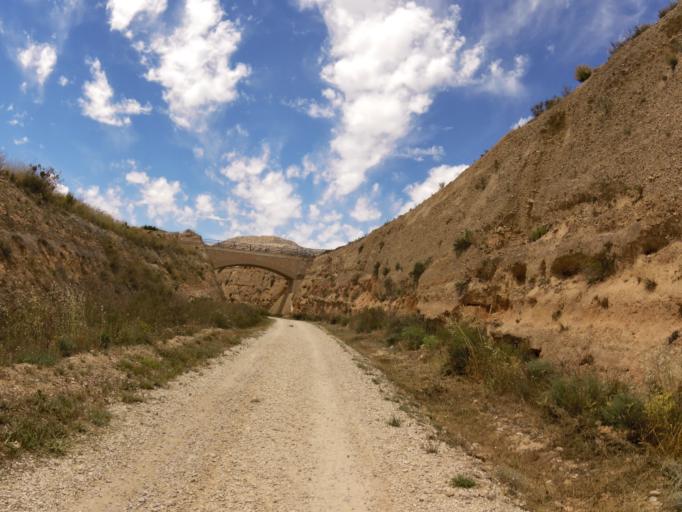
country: ES
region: Valencia
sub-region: Provincia de Alicante
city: Agost
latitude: 38.4516
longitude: -0.6698
